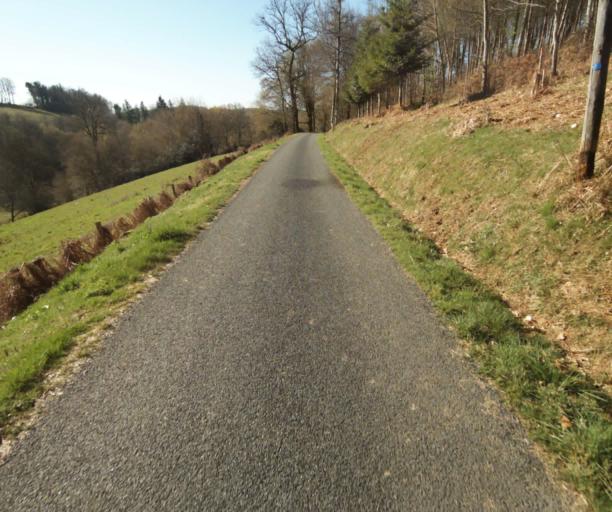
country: FR
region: Limousin
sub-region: Departement de la Correze
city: Seilhac
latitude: 45.3800
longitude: 1.7590
